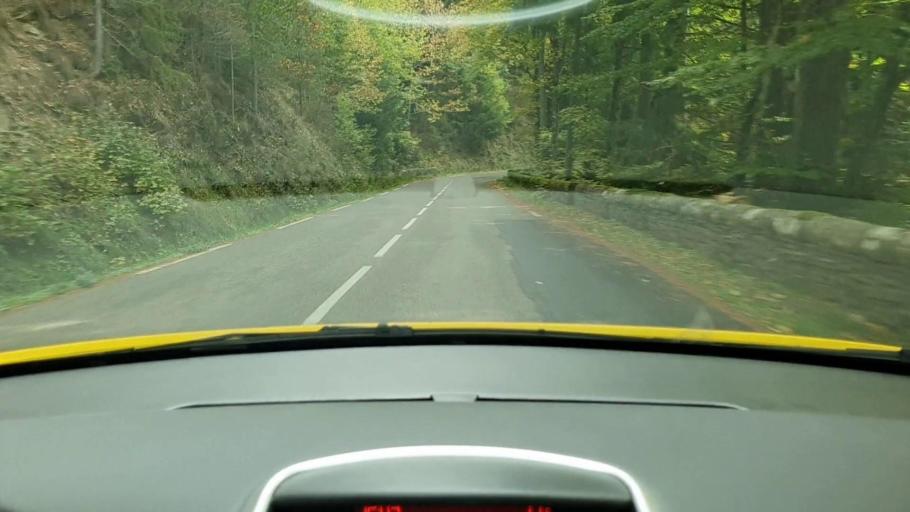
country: FR
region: Languedoc-Roussillon
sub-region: Departement de la Lozere
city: Meyrueis
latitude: 44.1319
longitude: 3.4313
